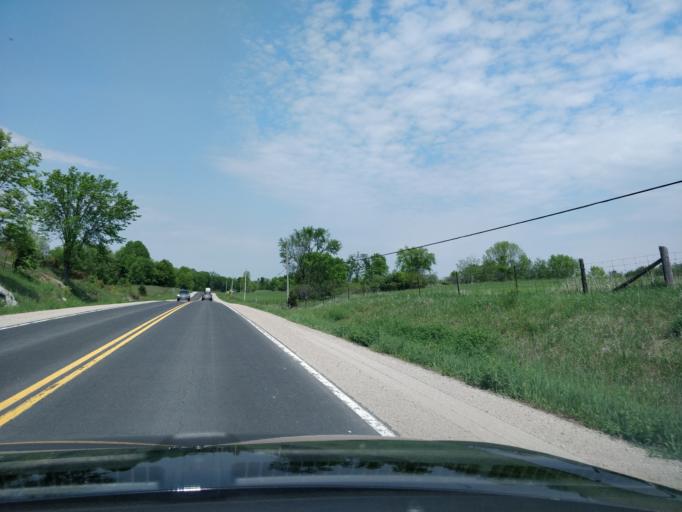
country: CA
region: Ontario
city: Perth
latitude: 44.7725
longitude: -76.3636
